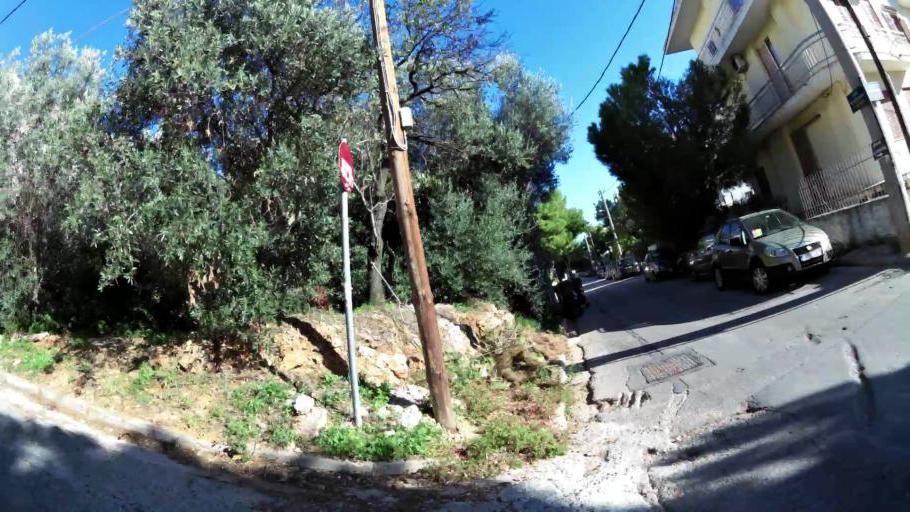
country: GR
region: Attica
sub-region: Nomarchia Athinas
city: Melissia
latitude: 38.0473
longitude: 23.8461
